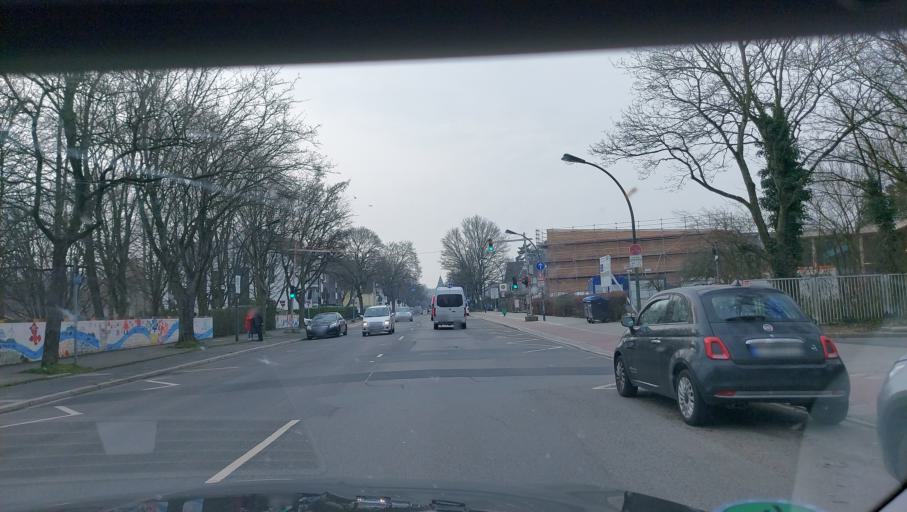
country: DE
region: North Rhine-Westphalia
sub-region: Regierungsbezirk Dusseldorf
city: Erkrath
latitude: 51.2432
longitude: 6.8583
